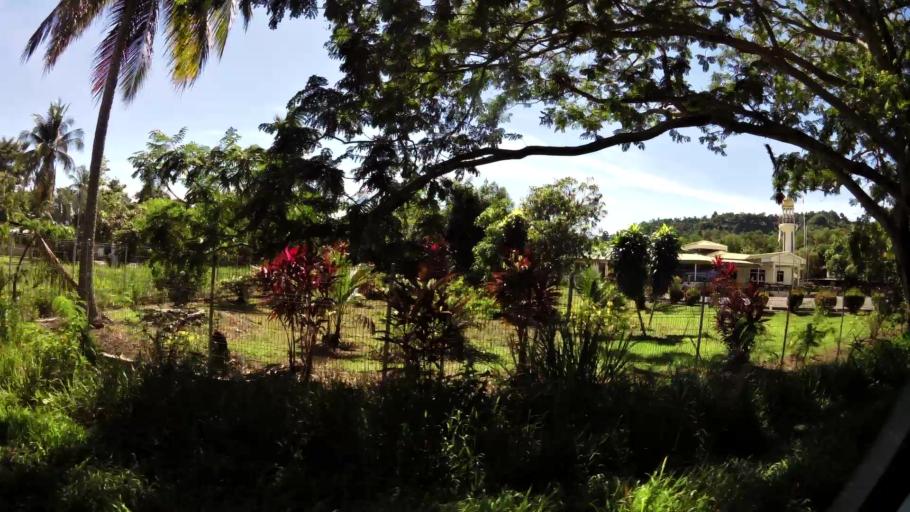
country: BN
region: Brunei and Muara
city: Bandar Seri Begawan
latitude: 5.0026
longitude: 115.0527
